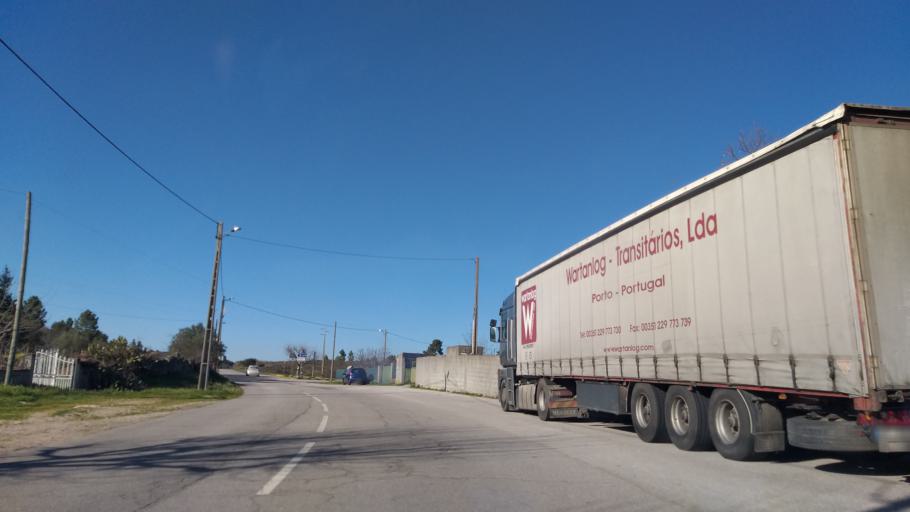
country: PT
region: Guarda
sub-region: Celorico da Beira
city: Celorico da Beira
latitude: 40.6109
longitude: -7.3622
